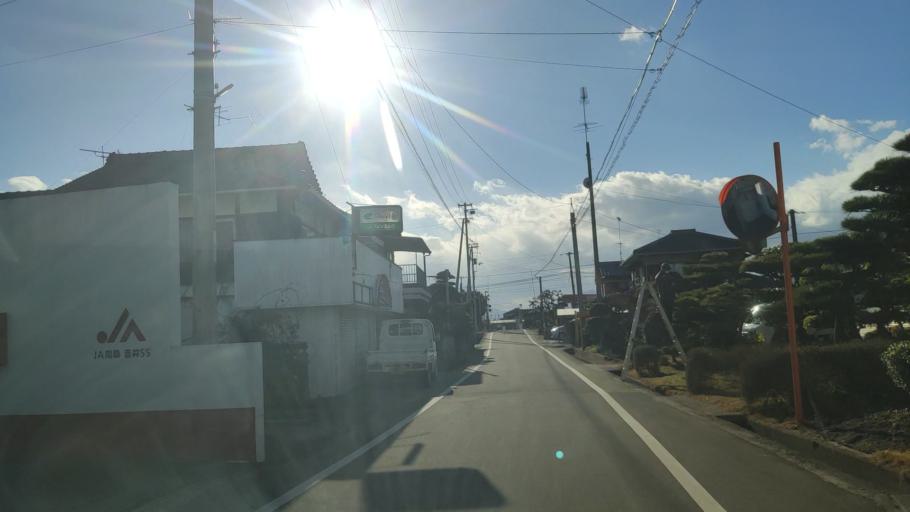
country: JP
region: Ehime
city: Saijo
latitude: 33.9129
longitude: 133.0998
